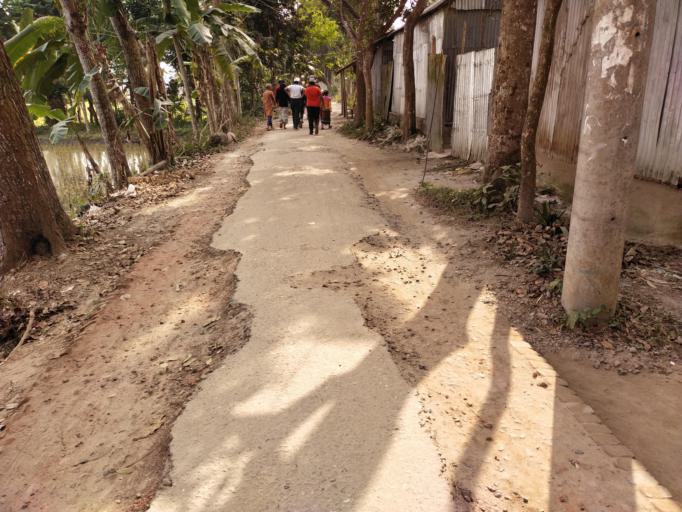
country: BD
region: Dhaka
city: Narsingdi
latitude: 24.0336
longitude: 90.7191
